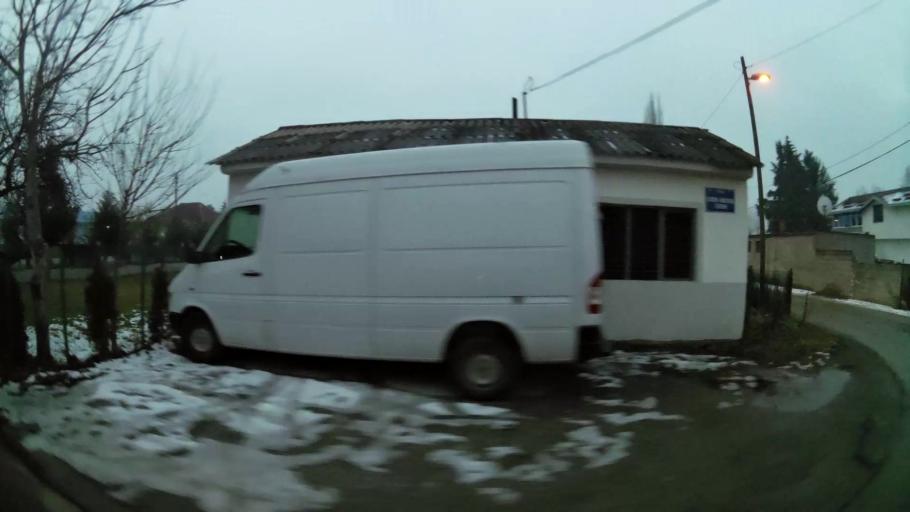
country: MK
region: Kisela Voda
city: Kisela Voda
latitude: 41.9733
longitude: 21.4911
